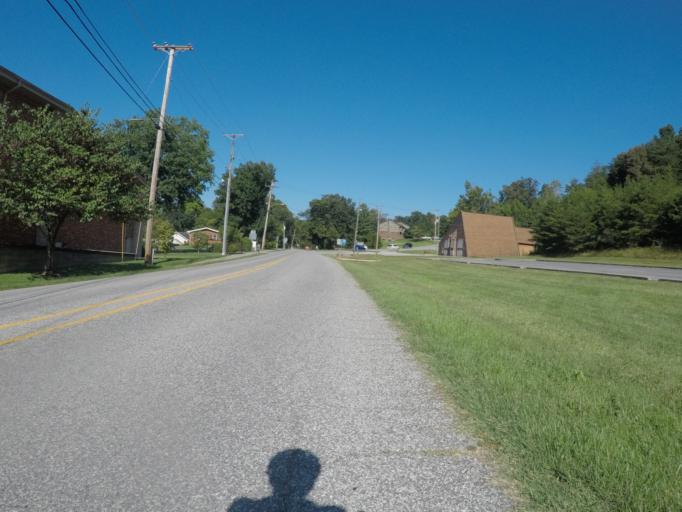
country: US
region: Kentucky
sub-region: Greenup County
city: Russell
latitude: 38.5055
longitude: -82.6938
